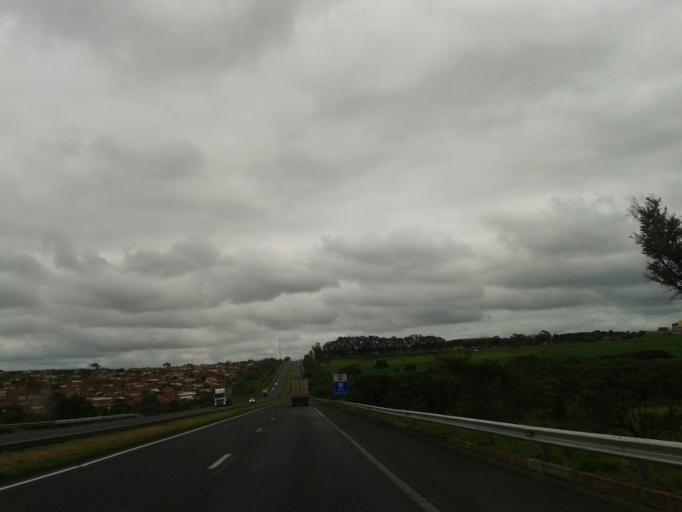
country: BR
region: Minas Gerais
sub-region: Uberlandia
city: Uberlandia
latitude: -18.9596
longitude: -48.2162
